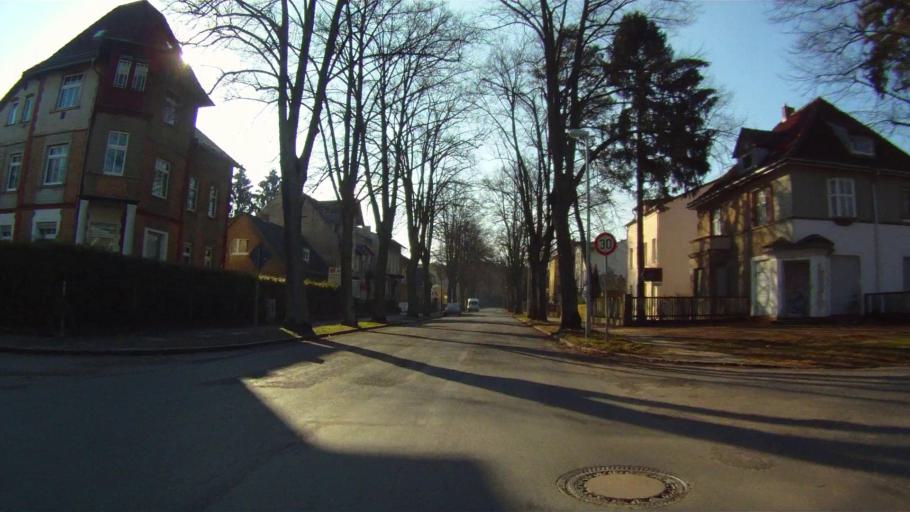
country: DE
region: Brandenburg
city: Schoneiche
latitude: 52.4572
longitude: 13.7025
